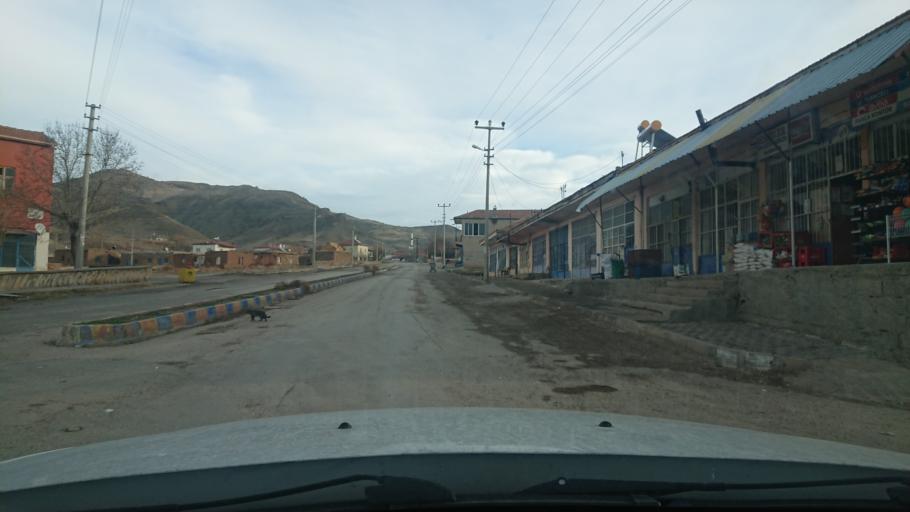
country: TR
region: Aksaray
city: Acipinar
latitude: 38.6143
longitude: 33.7814
